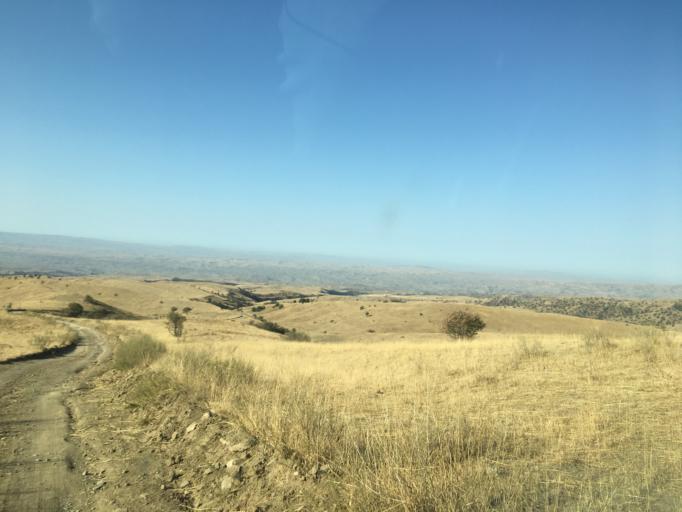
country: TM
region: Ahal
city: Baharly
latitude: 38.3351
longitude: 56.8904
